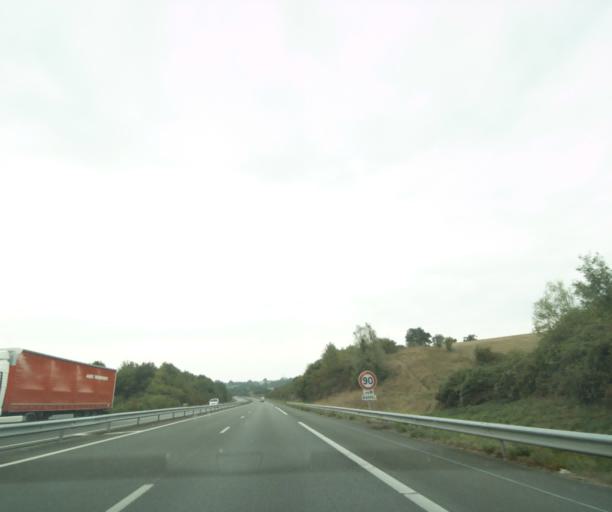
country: FR
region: Pays de la Loire
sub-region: Departement de la Vendee
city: Bournezeau
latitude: 46.6683
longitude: -1.1569
